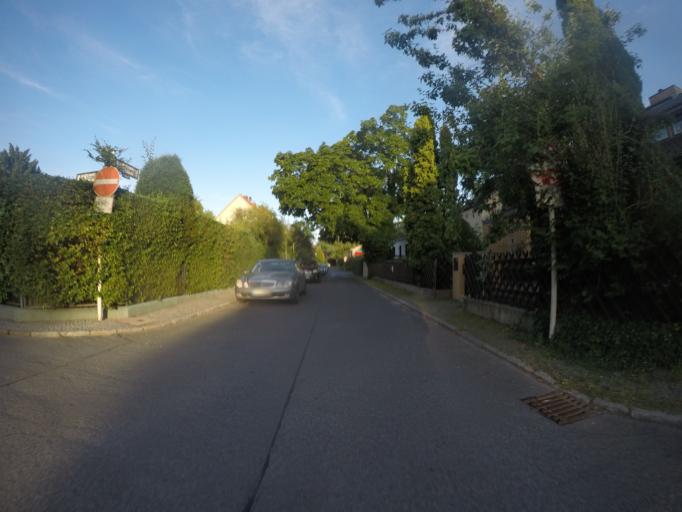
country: DE
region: Berlin
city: Grunewald
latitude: 52.4968
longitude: 13.2666
